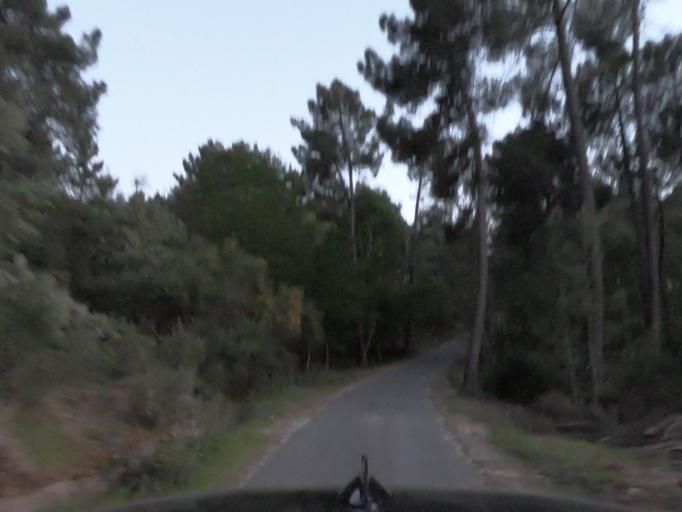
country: PT
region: Vila Real
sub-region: Vila Real
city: Vila Real
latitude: 41.3098
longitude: -7.6800
